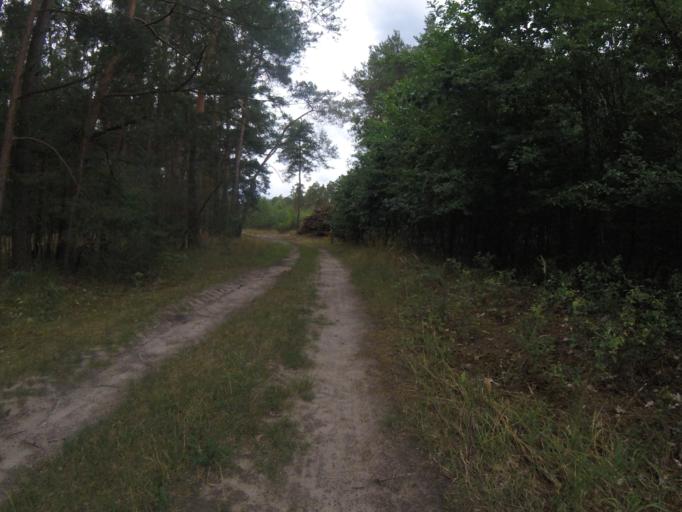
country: DE
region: Brandenburg
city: Bestensee
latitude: 52.2628
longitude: 13.7049
